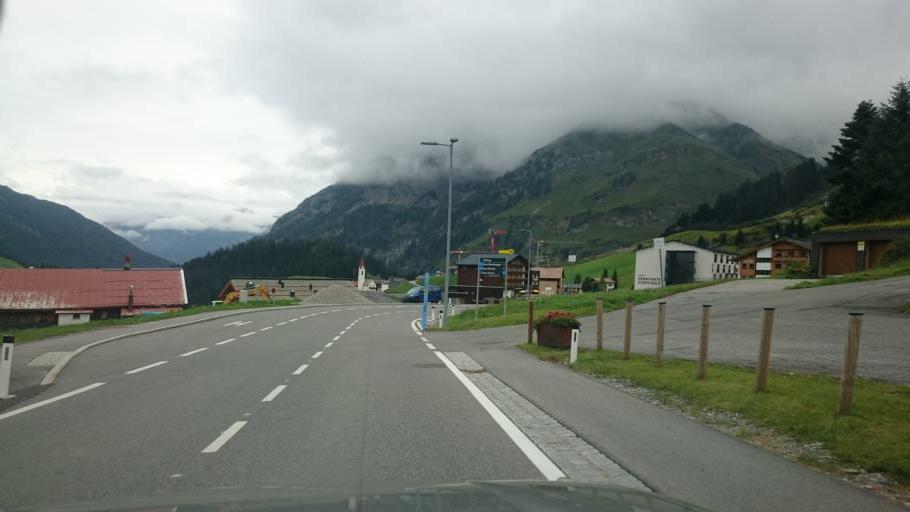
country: AT
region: Vorarlberg
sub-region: Politischer Bezirk Bregenz
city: Warth
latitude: 47.2622
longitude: 10.1742
